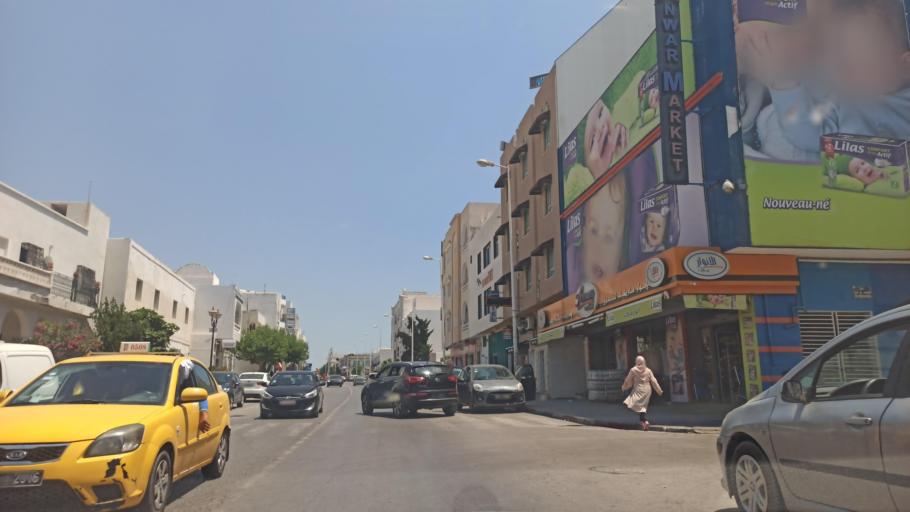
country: TN
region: Nabul
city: Al Hammamat
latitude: 36.4024
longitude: 10.6250
